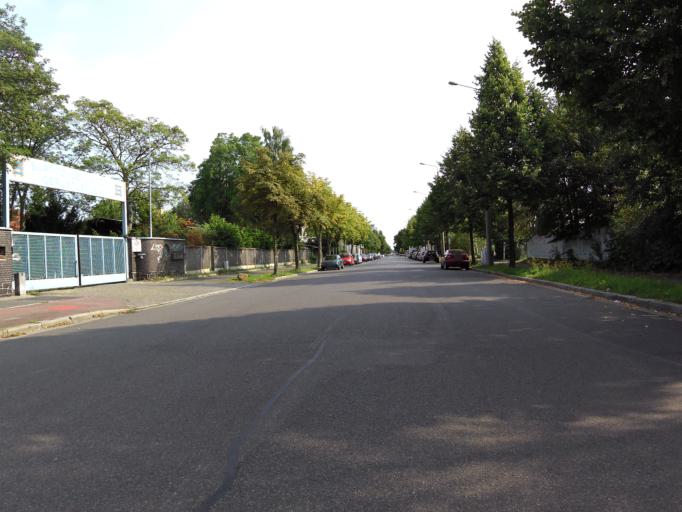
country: DE
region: Saxony
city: Rackwitz
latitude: 51.3867
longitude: 12.3903
